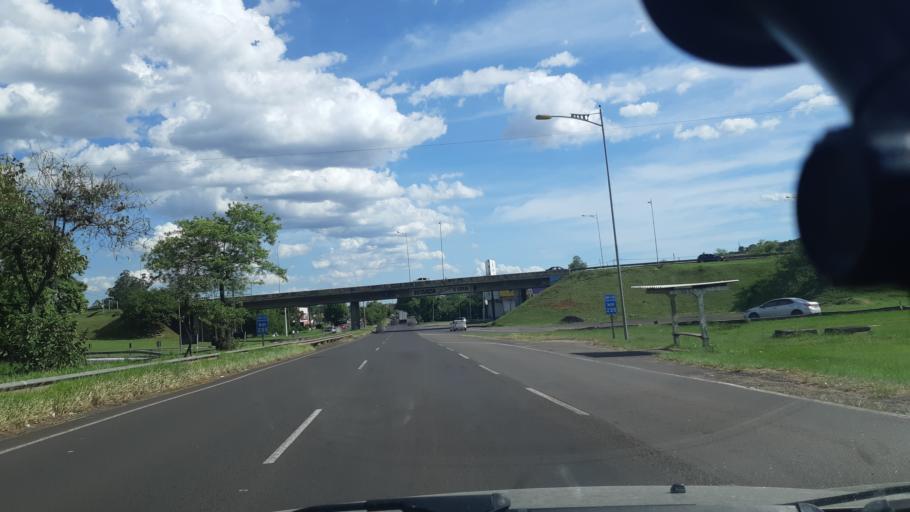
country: BR
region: Rio Grande do Sul
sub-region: Novo Hamburgo
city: Novo Hamburgo
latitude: -29.6562
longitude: -51.1444
